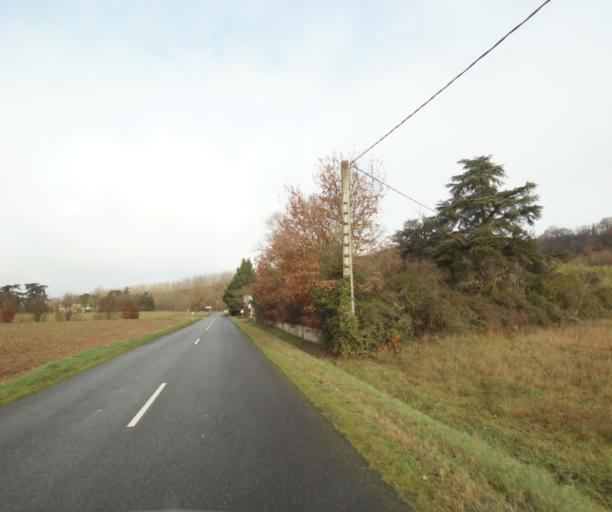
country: FR
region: Midi-Pyrenees
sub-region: Departement du Tarn-et-Garonne
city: Nohic
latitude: 43.8948
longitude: 1.4710
